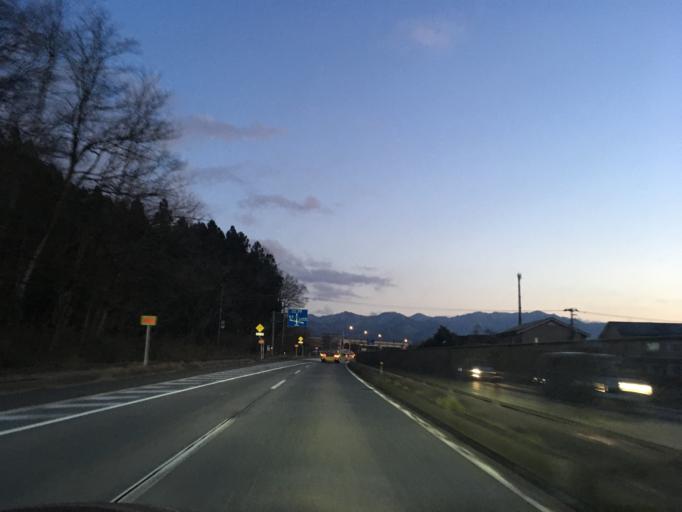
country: JP
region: Yamagata
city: Kaminoyama
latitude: 38.1411
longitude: 140.2870
